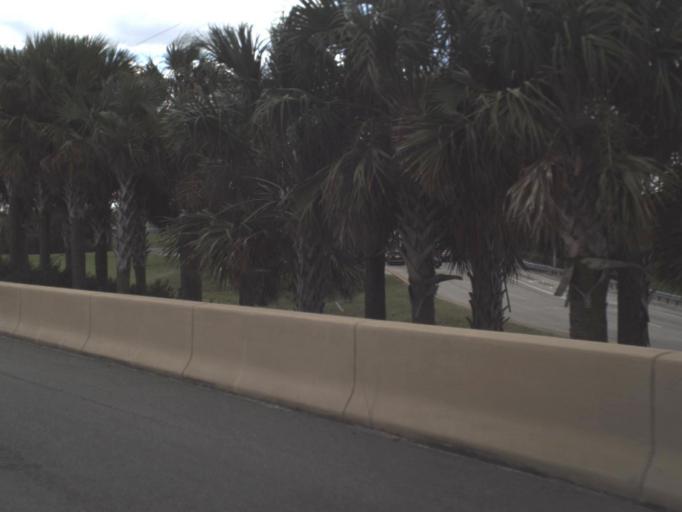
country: US
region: Florida
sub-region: Orange County
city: Tangelo Park
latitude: 28.4770
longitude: -81.4482
